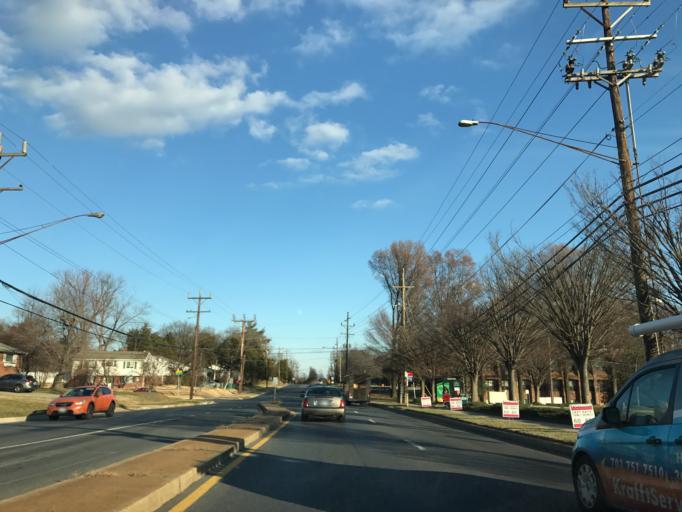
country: US
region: Maryland
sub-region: Montgomery County
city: North Bethesda
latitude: 39.0536
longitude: -77.1042
